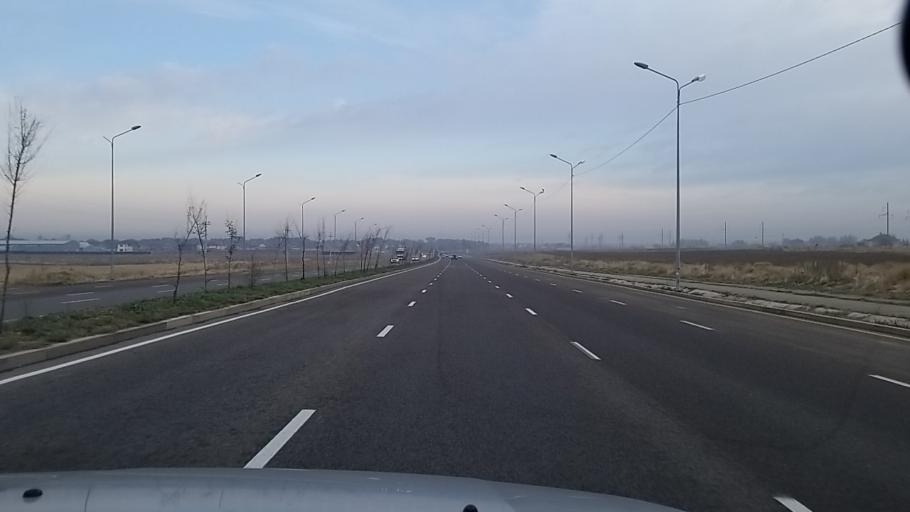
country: KZ
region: Almaty Oblysy
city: Burunday
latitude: 43.3430
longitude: 76.8338
